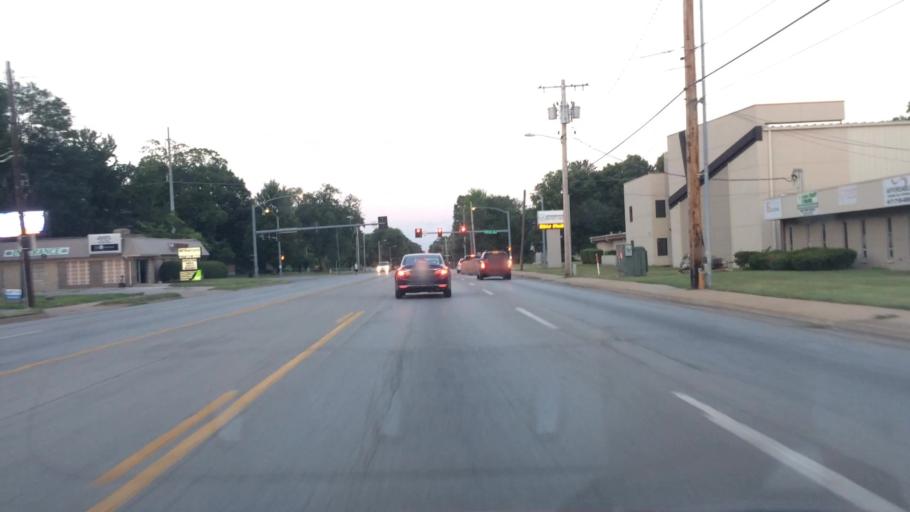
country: US
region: Missouri
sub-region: Greene County
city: Springfield
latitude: 37.1821
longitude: -93.2918
